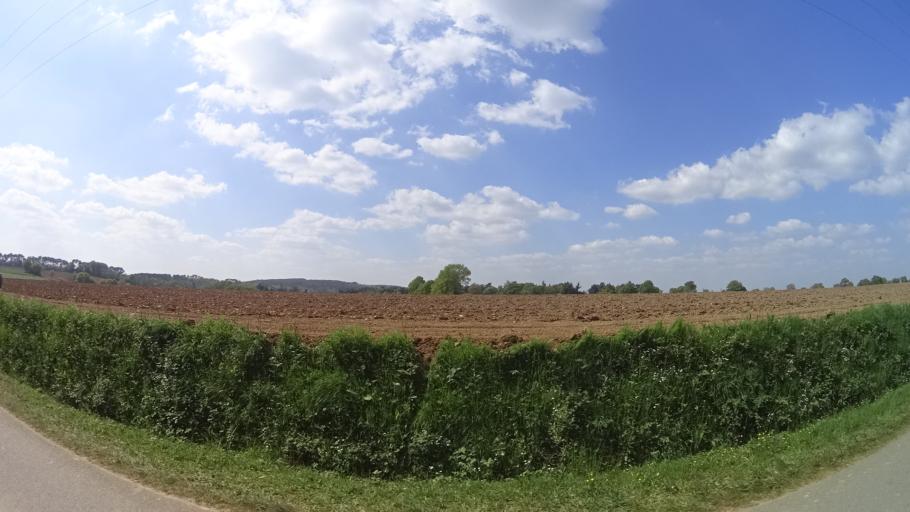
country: FR
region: Brittany
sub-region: Departement du Morbihan
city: Beganne
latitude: 47.5896
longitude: -2.2822
